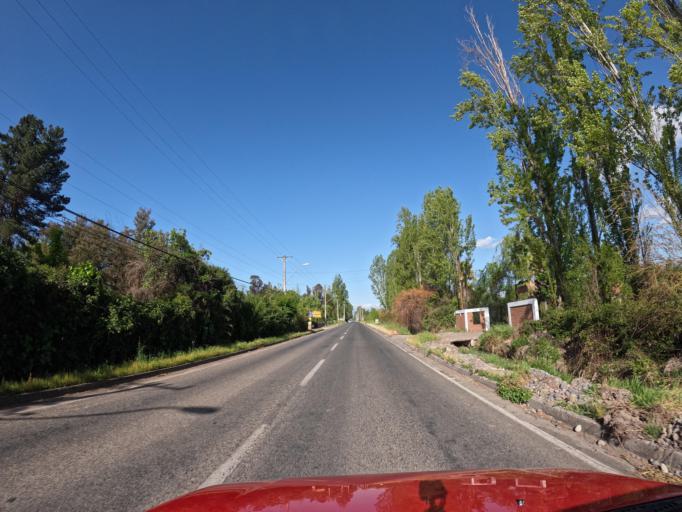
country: CL
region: Maule
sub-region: Provincia de Curico
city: Teno
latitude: -34.8684
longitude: -71.2440
